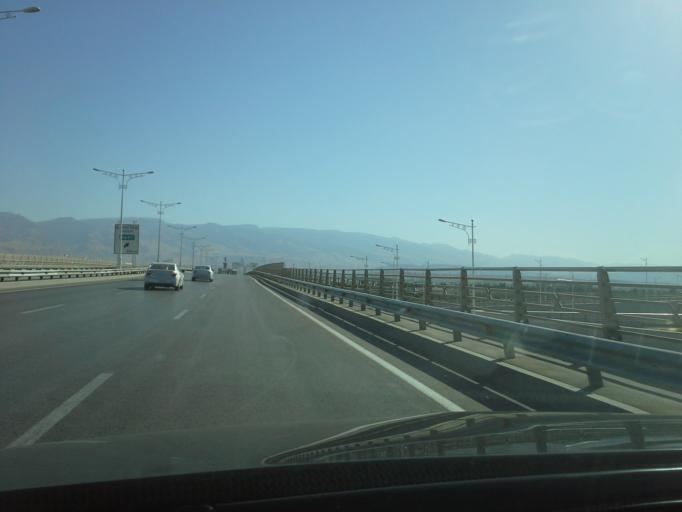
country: TM
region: Ahal
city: Ashgabat
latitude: 37.9785
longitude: 58.3962
